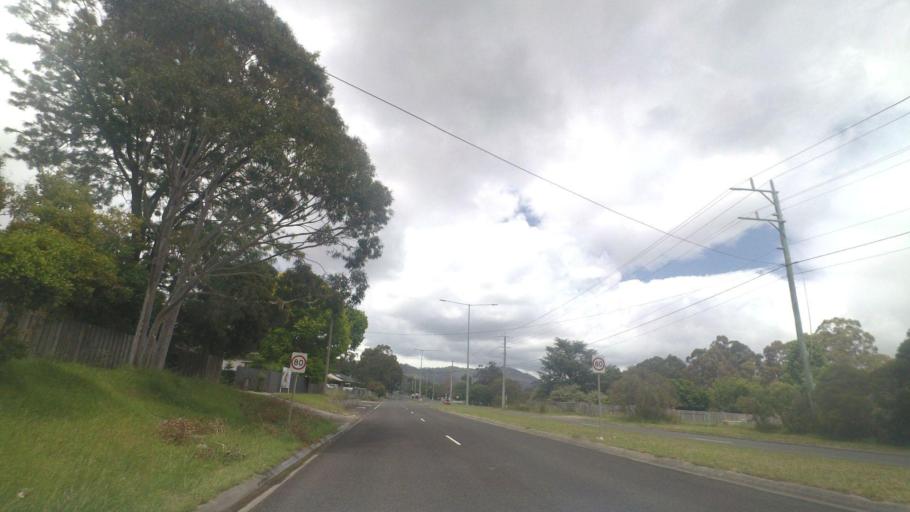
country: AU
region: Victoria
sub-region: Yarra Ranges
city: Mount Evelyn
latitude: -37.7743
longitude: 145.3631
